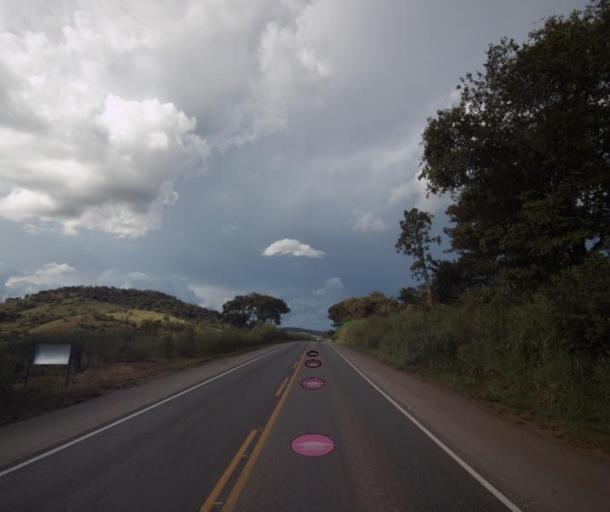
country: BR
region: Goias
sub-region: Rialma
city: Rialma
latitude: -15.2857
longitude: -49.5643
